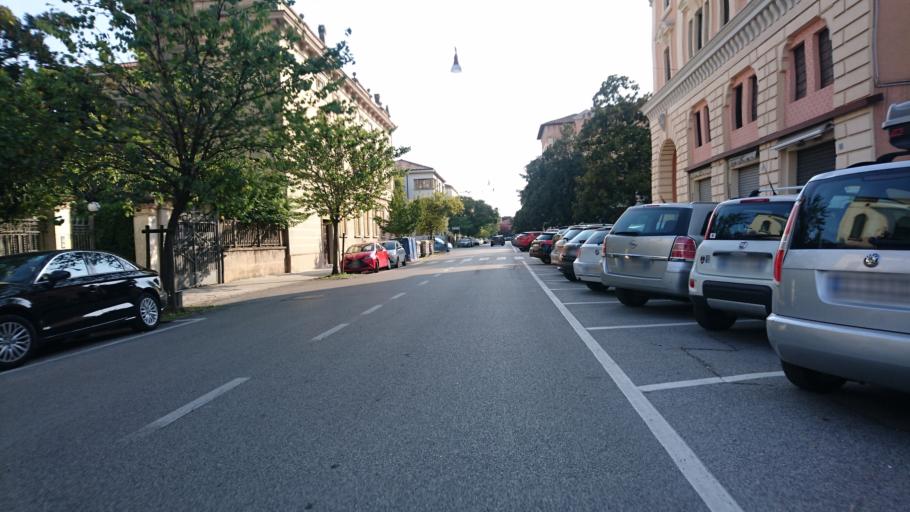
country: IT
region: Veneto
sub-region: Provincia di Padova
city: Padova
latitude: 45.3967
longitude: 11.8707
